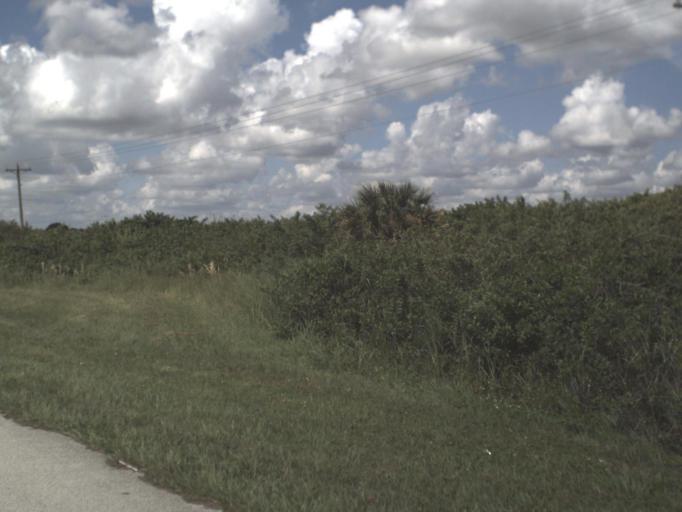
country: US
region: Florida
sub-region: Collier County
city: Immokalee
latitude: 26.5089
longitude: -81.5261
